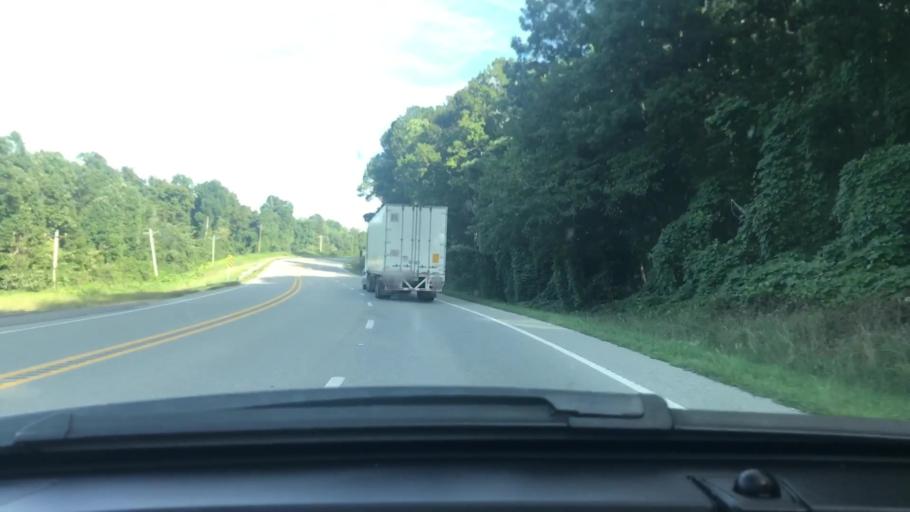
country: US
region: Arkansas
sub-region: Sharp County
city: Cherokee Village
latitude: 36.3006
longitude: -91.4096
